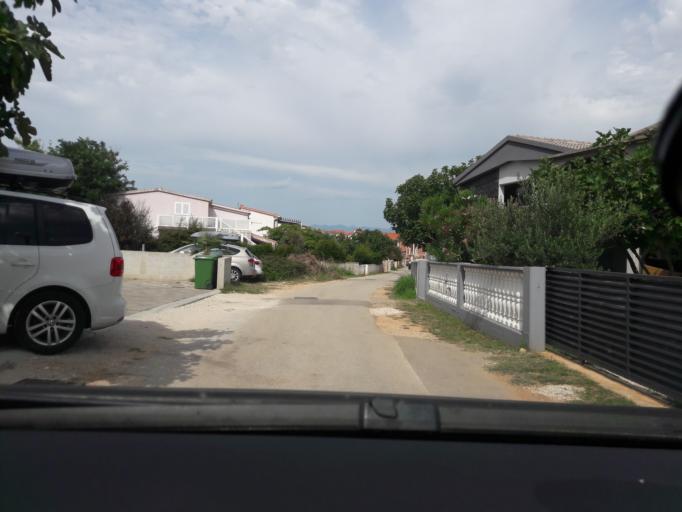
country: HR
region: Zadarska
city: Vir
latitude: 44.2978
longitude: 15.0789
